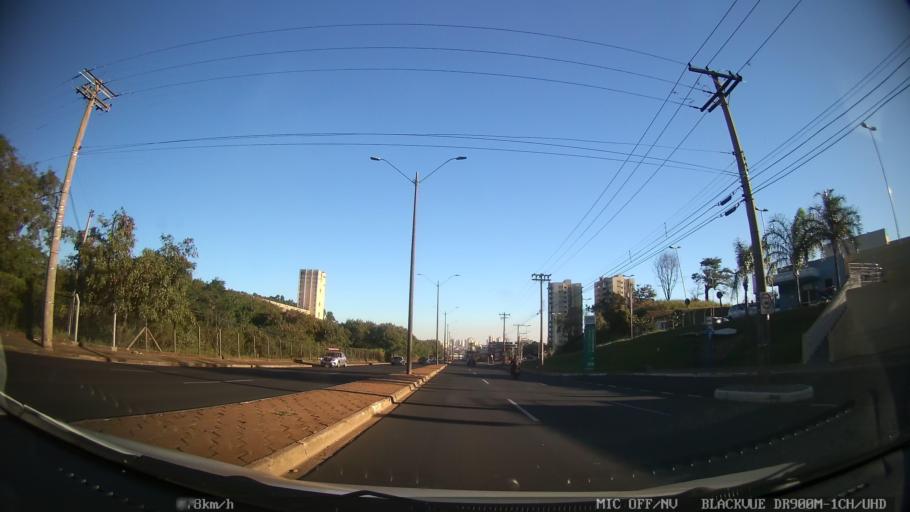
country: BR
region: Sao Paulo
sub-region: Araraquara
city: Araraquara
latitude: -21.7740
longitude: -48.1669
